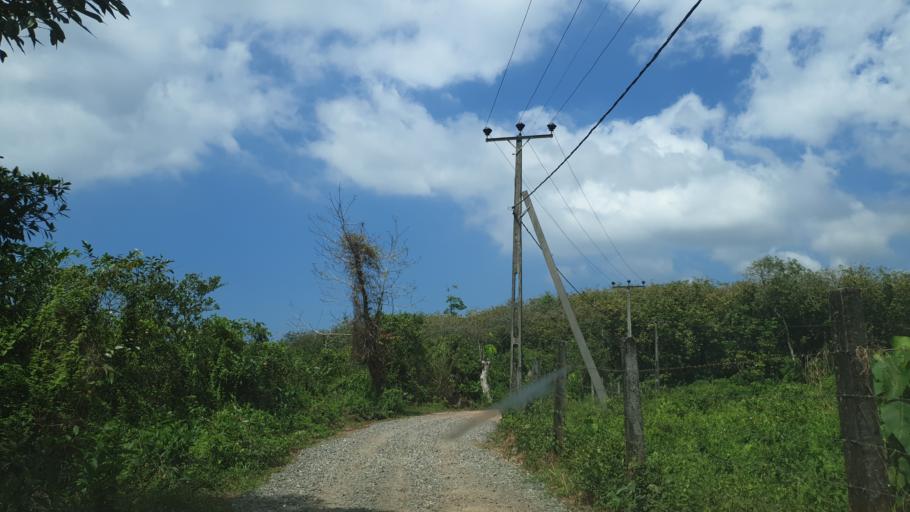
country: LK
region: Western
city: Panadura
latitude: 6.6785
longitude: 79.9612
